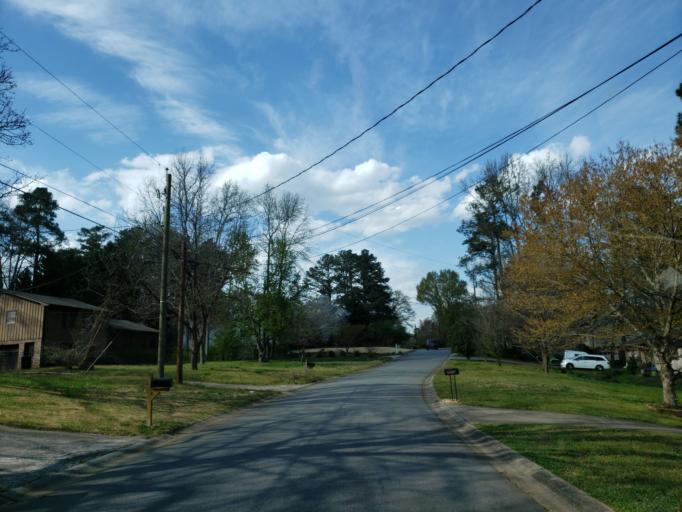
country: US
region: Georgia
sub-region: Cherokee County
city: Woodstock
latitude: 34.0224
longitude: -84.4778
